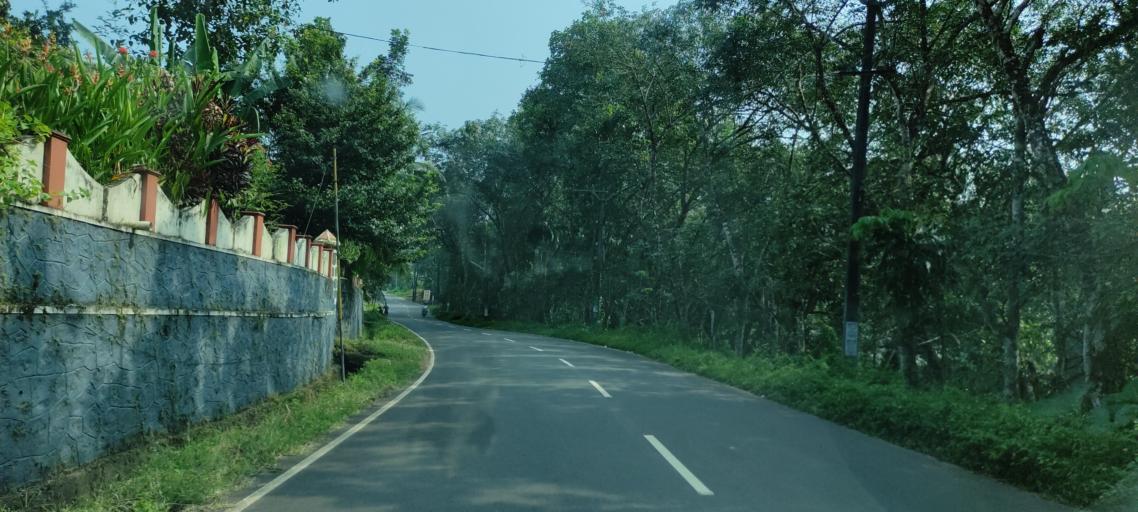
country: IN
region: Kerala
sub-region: Pattanamtitta
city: Adur
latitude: 9.2371
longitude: 76.6856
